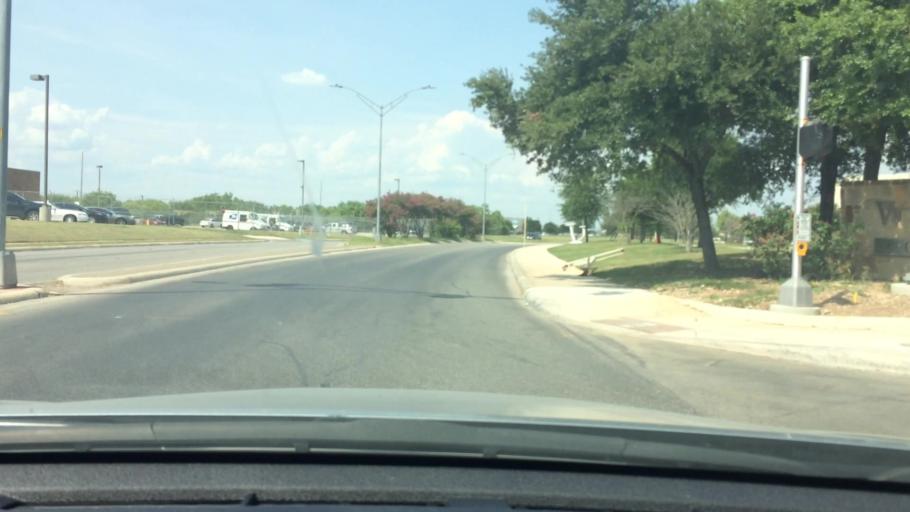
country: US
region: Texas
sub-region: Bexar County
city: Leon Valley
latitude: 29.4422
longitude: -98.6566
